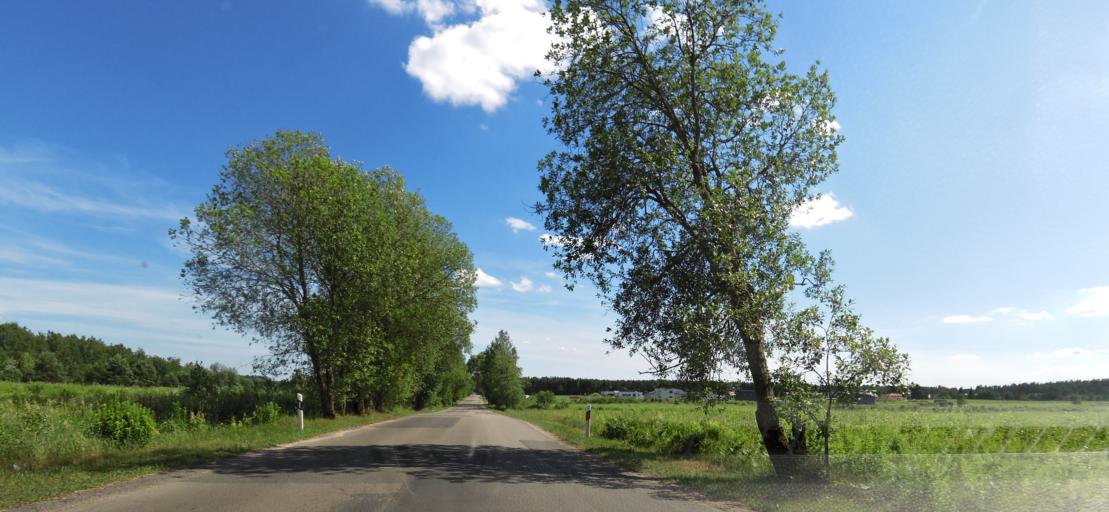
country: LT
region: Vilnius County
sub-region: Vilnius
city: Fabijoniskes
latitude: 54.8108
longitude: 25.3240
